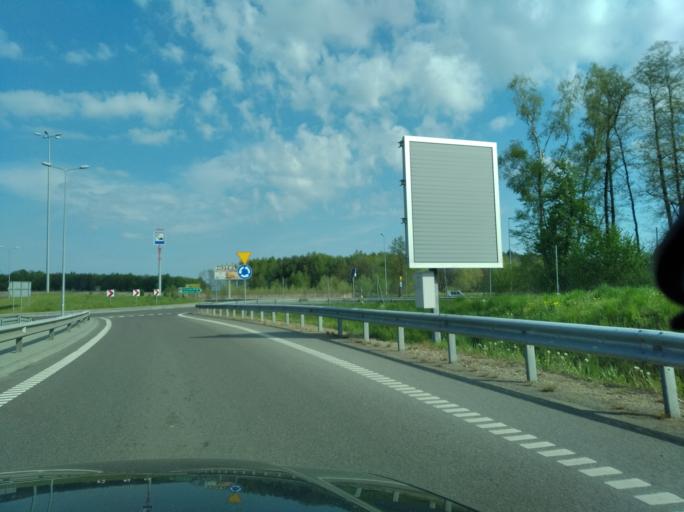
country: PL
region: Subcarpathian Voivodeship
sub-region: Powiat lubaczowski
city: Wielkie Oczy
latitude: 49.9661
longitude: 23.0680
